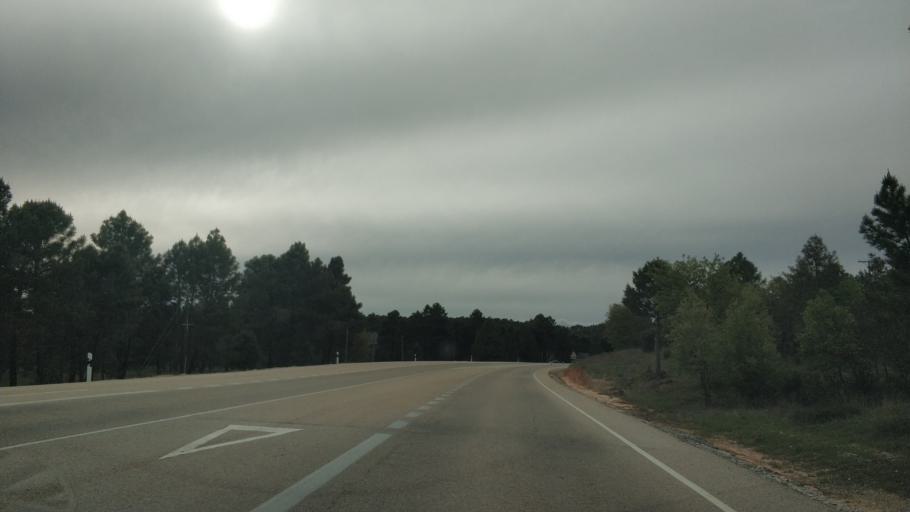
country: ES
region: Castille and Leon
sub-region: Provincia de Soria
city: Bayubas de Abajo
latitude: 41.5119
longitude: -2.9235
